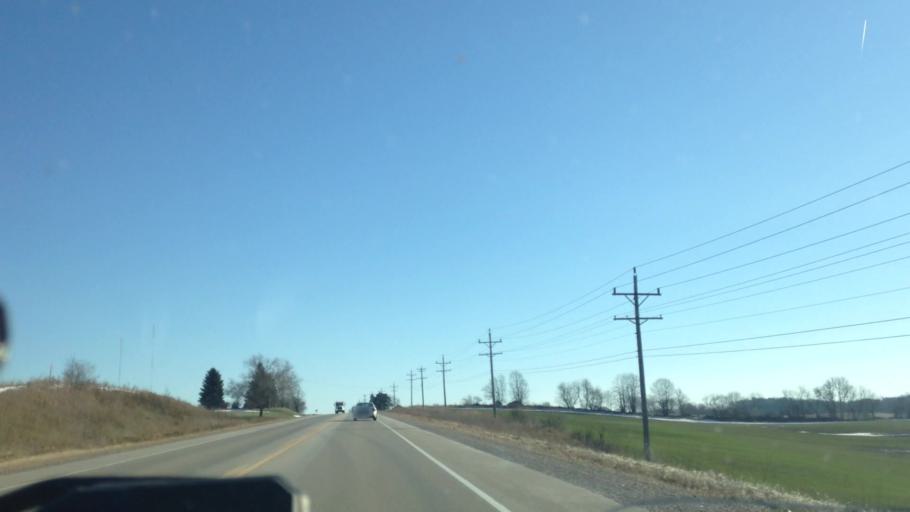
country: US
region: Wisconsin
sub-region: Washington County
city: Slinger
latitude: 43.4274
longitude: -88.3156
